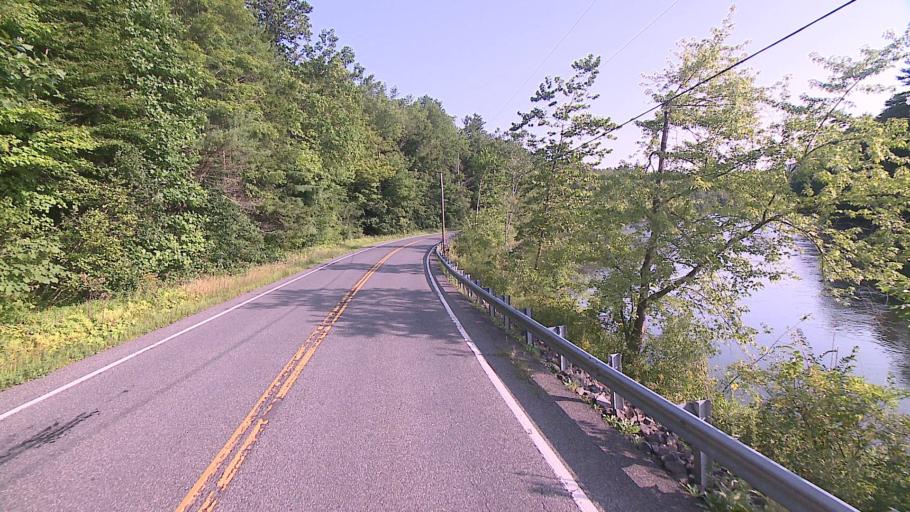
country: US
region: Connecticut
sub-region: Litchfield County
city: Kent
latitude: 41.8304
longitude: -73.3846
